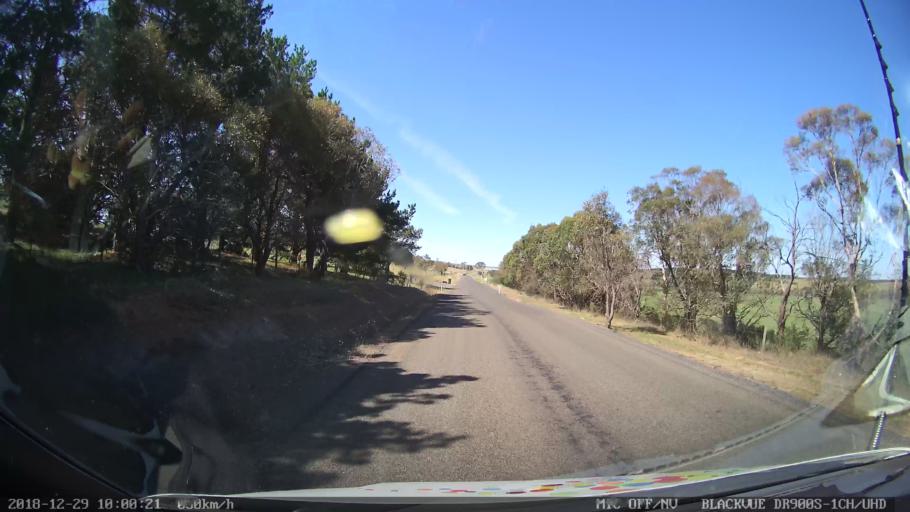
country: AU
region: New South Wales
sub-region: Goulburn Mulwaree
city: Goulburn
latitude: -34.7915
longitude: 149.4860
